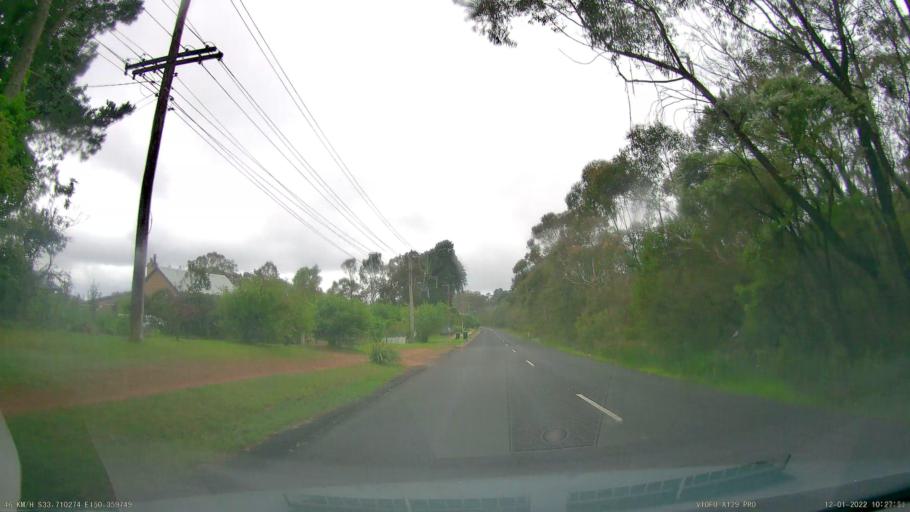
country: AU
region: New South Wales
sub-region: Blue Mountains Municipality
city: Leura
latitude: -33.7103
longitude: 150.3600
